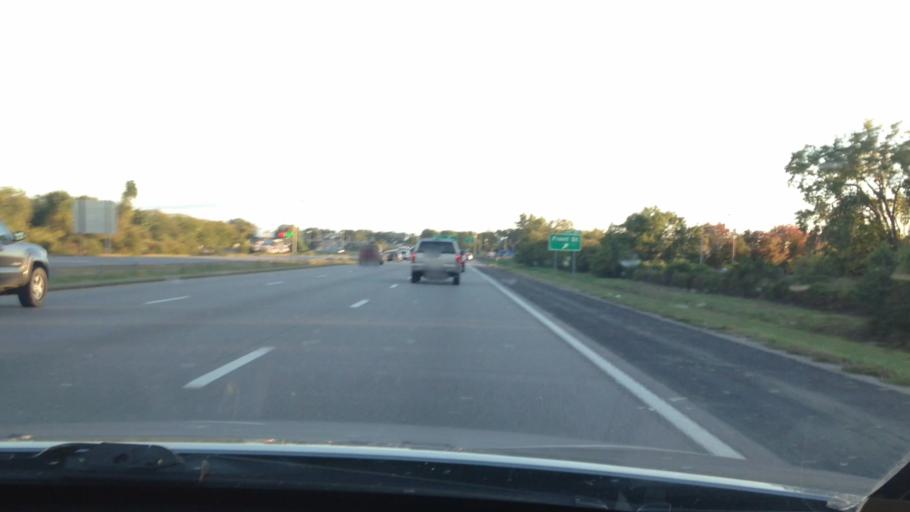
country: US
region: Missouri
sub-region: Jackson County
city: Sugar Creek
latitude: 39.1372
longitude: -94.4990
